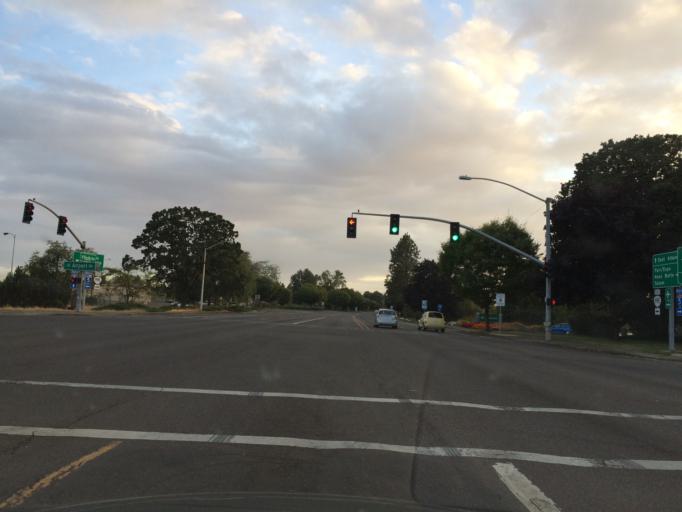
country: US
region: Oregon
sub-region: Linn County
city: Millersburg
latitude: 44.6419
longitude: -123.0662
